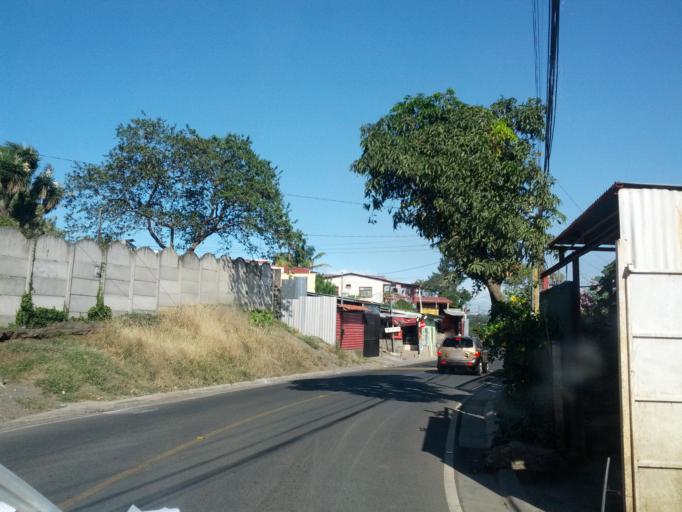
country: CR
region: Alajuela
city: Alajuela
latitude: 9.9784
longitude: -84.2277
